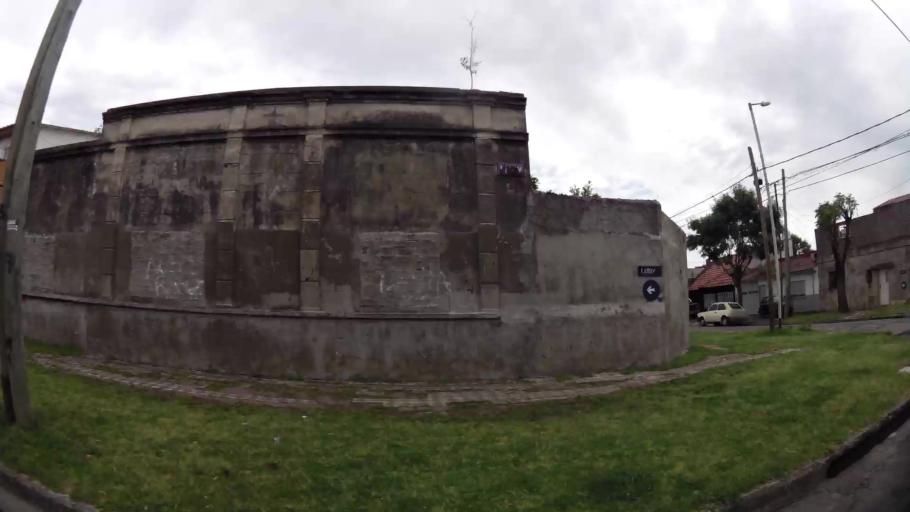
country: AR
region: Buenos Aires
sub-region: Partido de Avellaneda
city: Avellaneda
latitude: -34.6796
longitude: -58.3754
